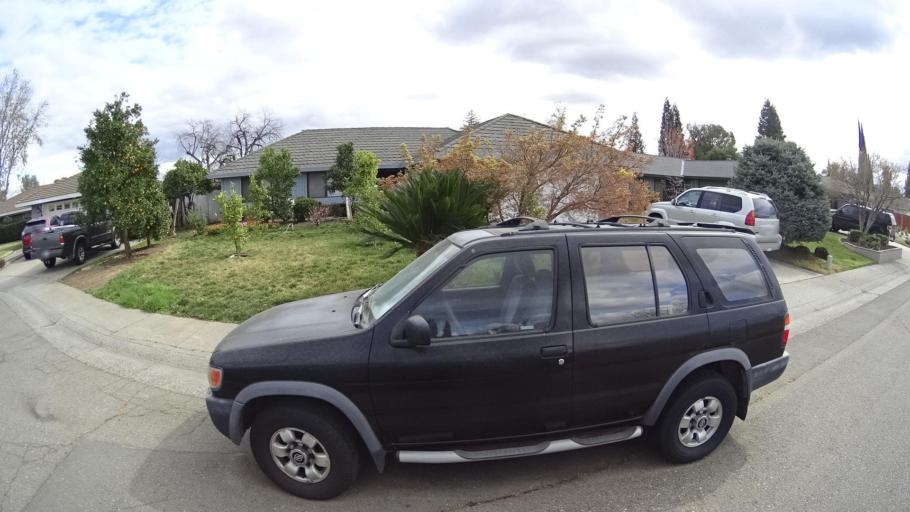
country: US
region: California
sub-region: Sacramento County
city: Rancho Cordova
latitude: 38.6055
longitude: -121.2788
